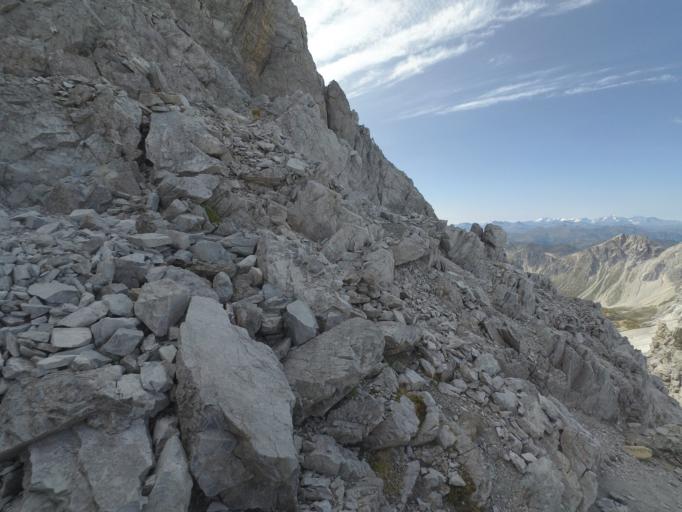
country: AT
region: Salzburg
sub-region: Politischer Bezirk Sankt Johann im Pongau
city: Kleinarl
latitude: 47.2065
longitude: 13.3943
